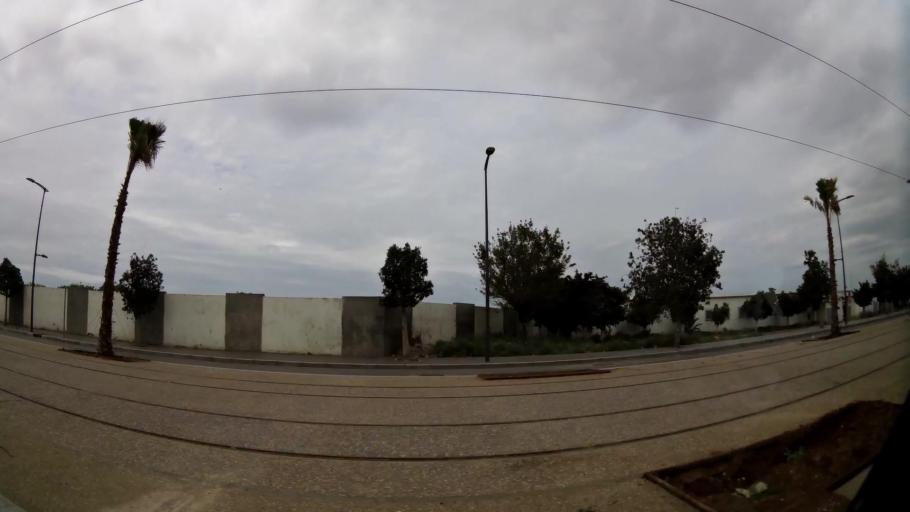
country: MA
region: Grand Casablanca
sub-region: Casablanca
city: Casablanca
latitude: 33.5781
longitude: -7.5713
